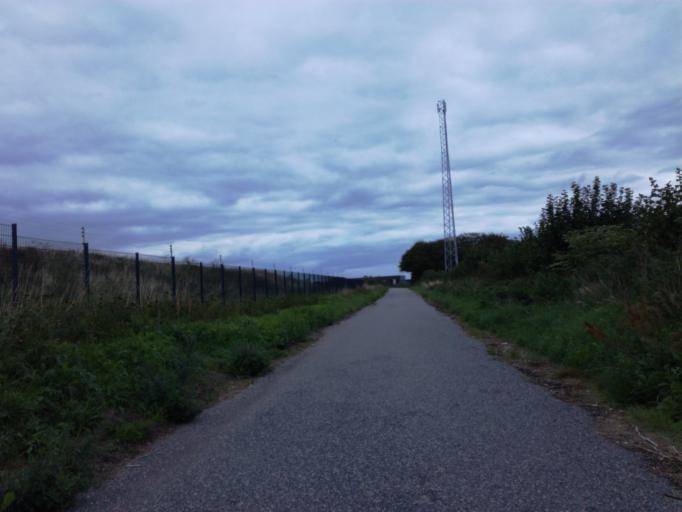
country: DK
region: South Denmark
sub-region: Vejle Kommune
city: Borkop
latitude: 55.6697
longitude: 9.5908
